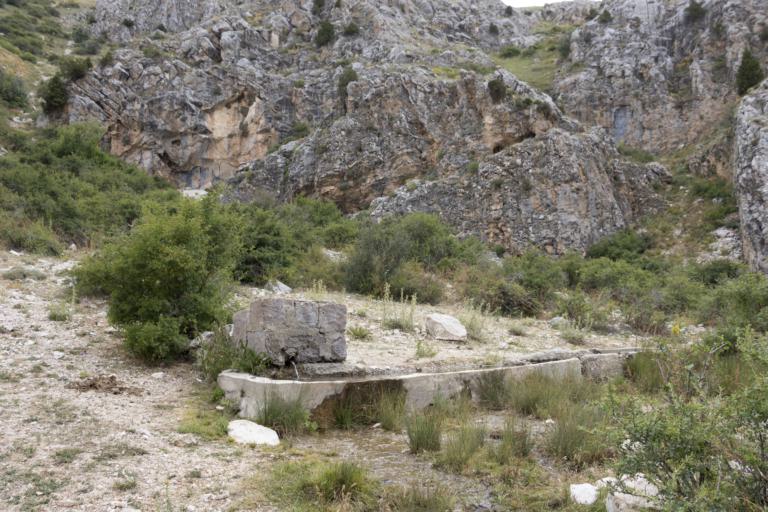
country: TR
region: Kayseri
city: Toklar
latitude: 38.4330
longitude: 36.1613
